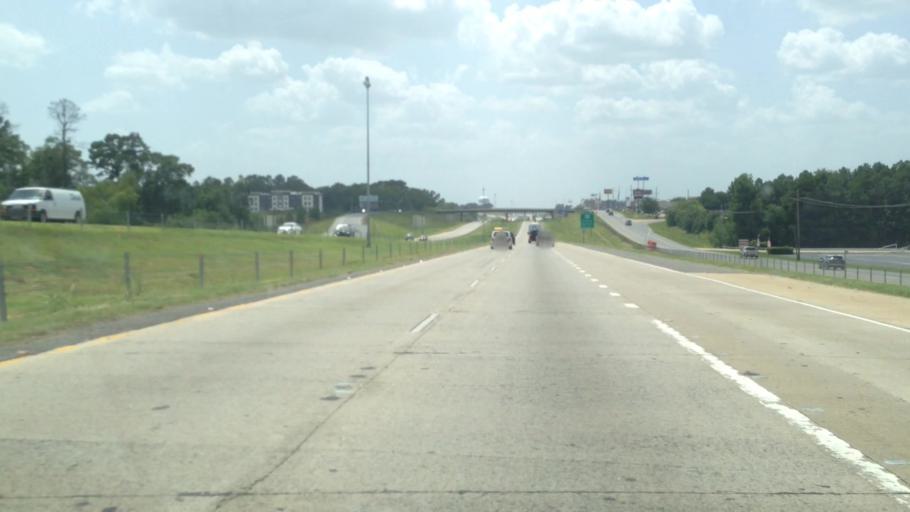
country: US
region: Louisiana
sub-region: Lincoln Parish
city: Ruston
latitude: 32.5404
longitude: -92.6193
